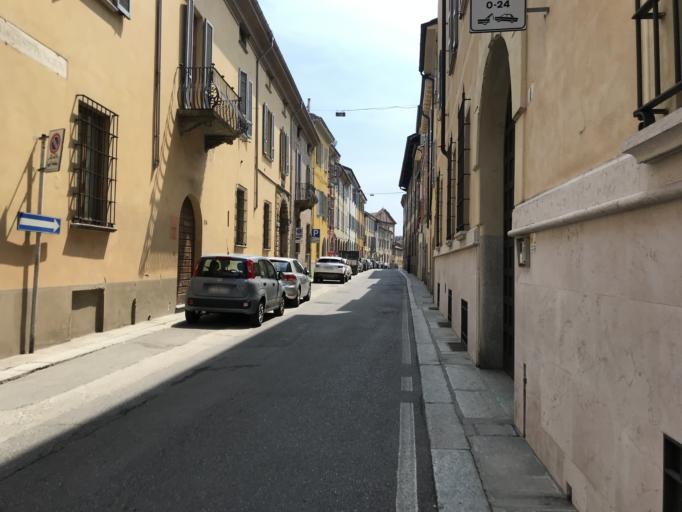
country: IT
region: Emilia-Romagna
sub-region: Provincia di Piacenza
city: Piacenza
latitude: 45.0499
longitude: 9.6992
